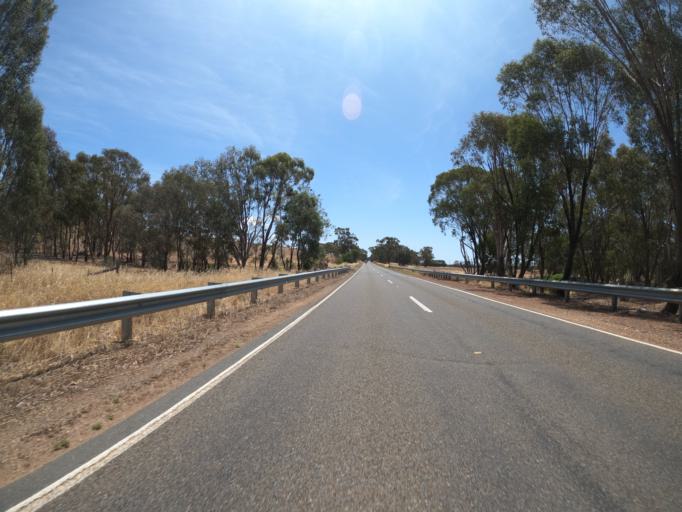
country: AU
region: Victoria
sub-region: Benalla
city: Benalla
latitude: -36.3284
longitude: 145.9612
